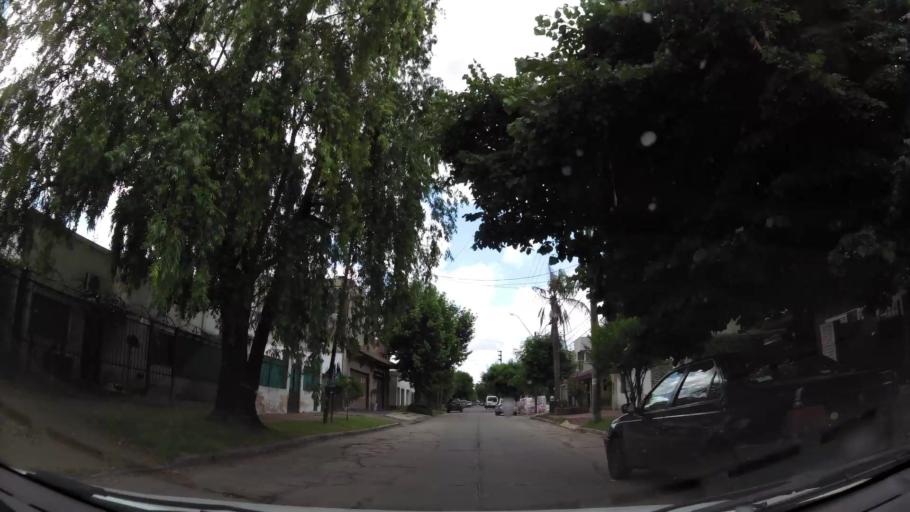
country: AR
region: Buenos Aires
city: Ituzaingo
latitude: -34.6530
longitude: -58.6655
